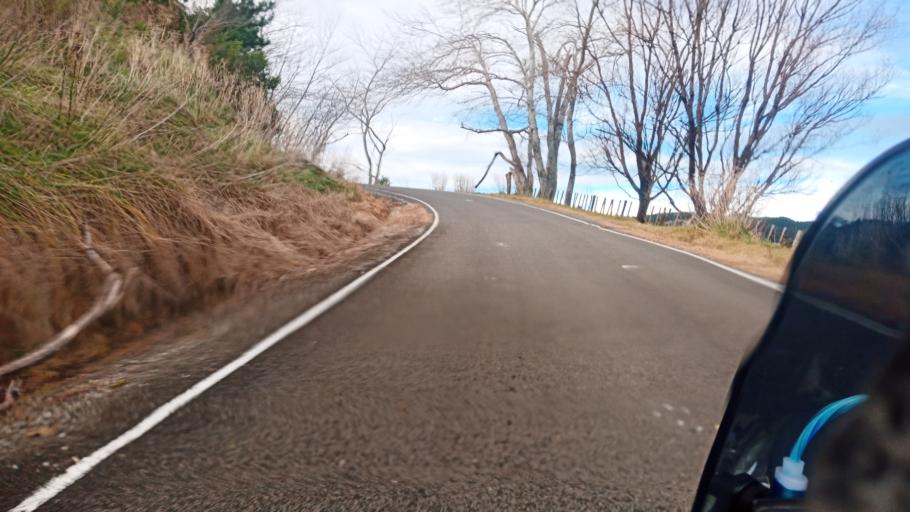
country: NZ
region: Gisborne
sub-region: Gisborne District
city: Gisborne
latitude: -38.4038
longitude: 177.9543
